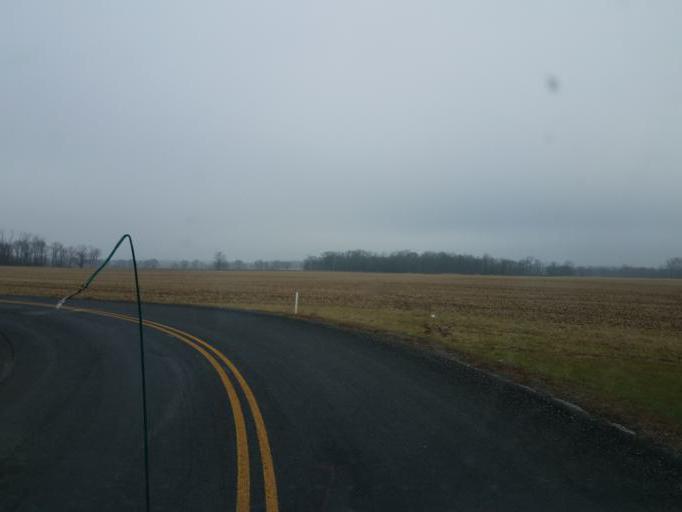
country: US
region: Ohio
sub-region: Champaign County
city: North Lewisburg
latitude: 40.2343
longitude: -83.5419
